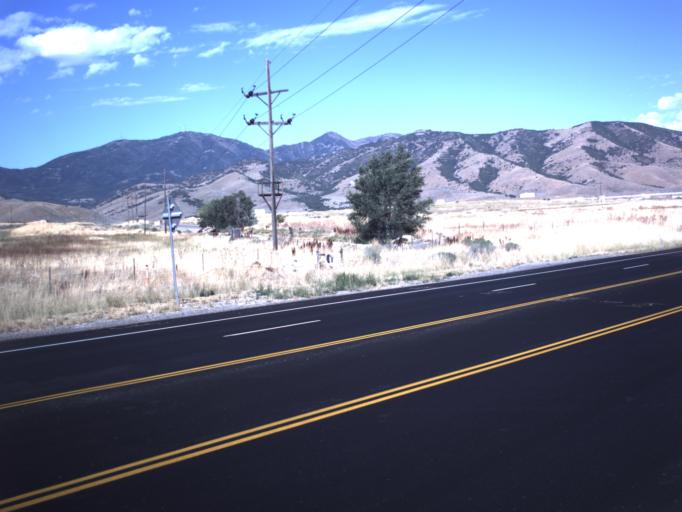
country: US
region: Utah
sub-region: Salt Lake County
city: Oquirrh
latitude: 40.6528
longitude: -112.0746
